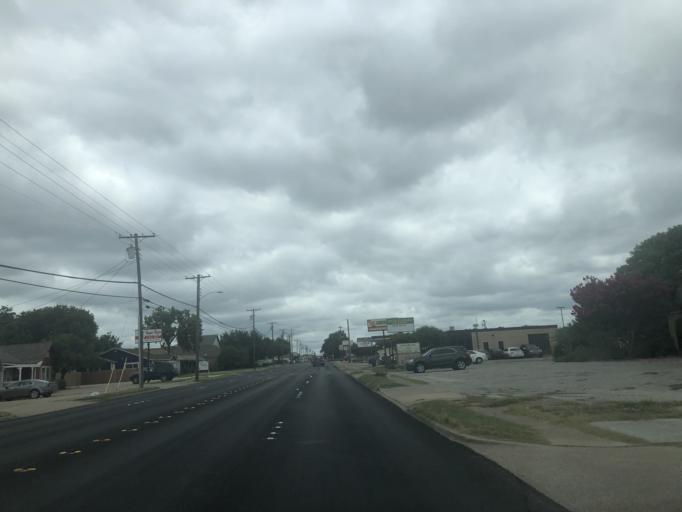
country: US
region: Texas
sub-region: Dallas County
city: Duncanville
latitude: 32.6399
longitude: -96.9084
